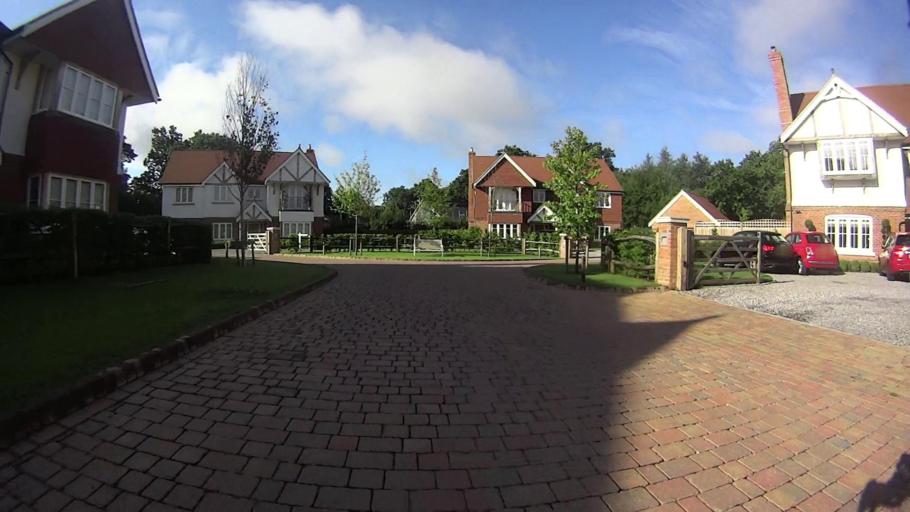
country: GB
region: England
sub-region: Surrey
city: Felbridge
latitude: 51.1363
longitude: -0.0577
